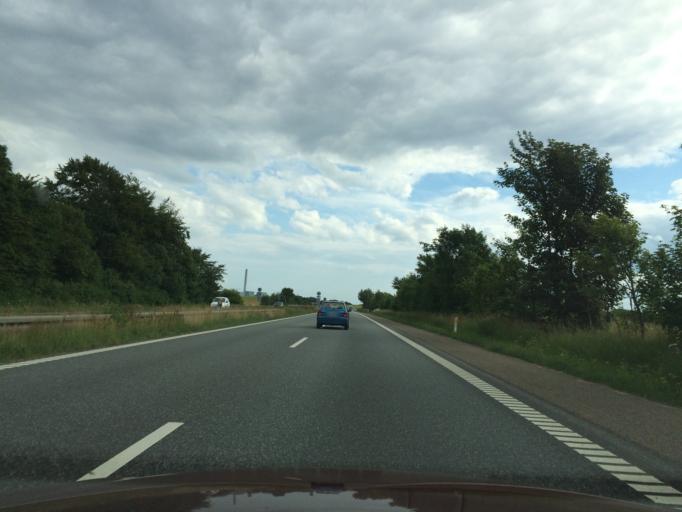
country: DK
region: Central Jutland
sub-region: Arhus Kommune
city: Logten
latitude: 56.2811
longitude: 10.3308
